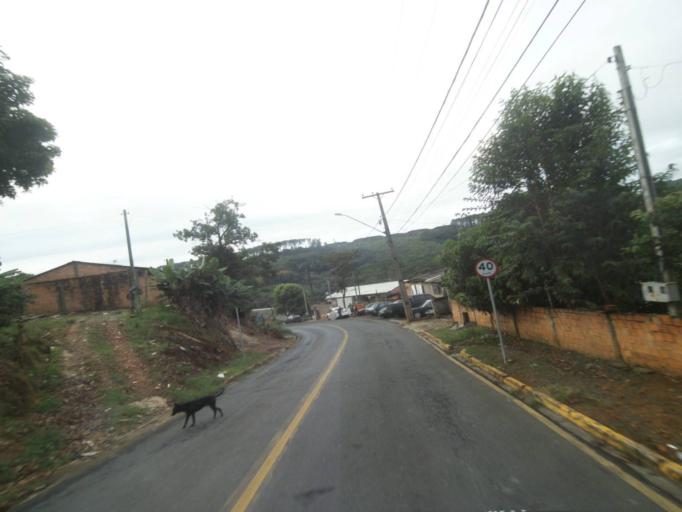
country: BR
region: Parana
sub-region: Telemaco Borba
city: Telemaco Borba
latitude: -24.3145
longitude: -50.6180
